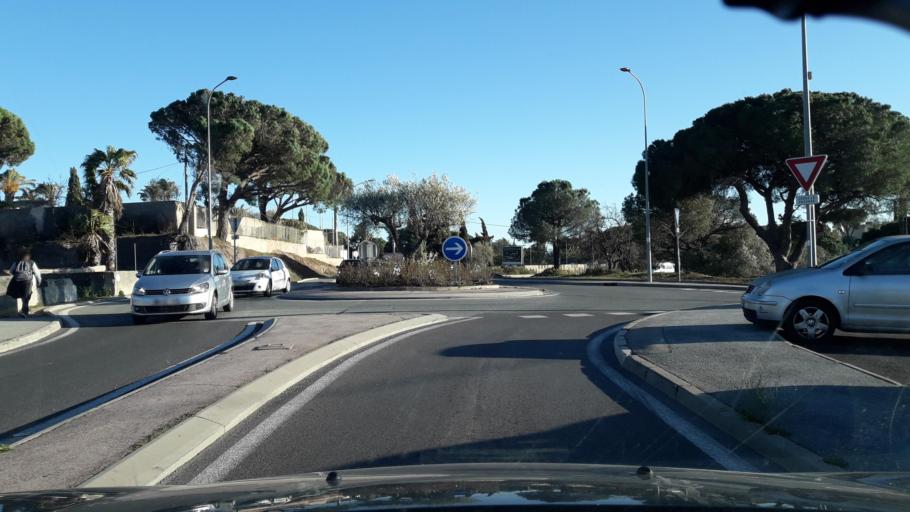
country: FR
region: Provence-Alpes-Cote d'Azur
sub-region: Departement du Var
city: Frejus
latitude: 43.4502
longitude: 6.7277
